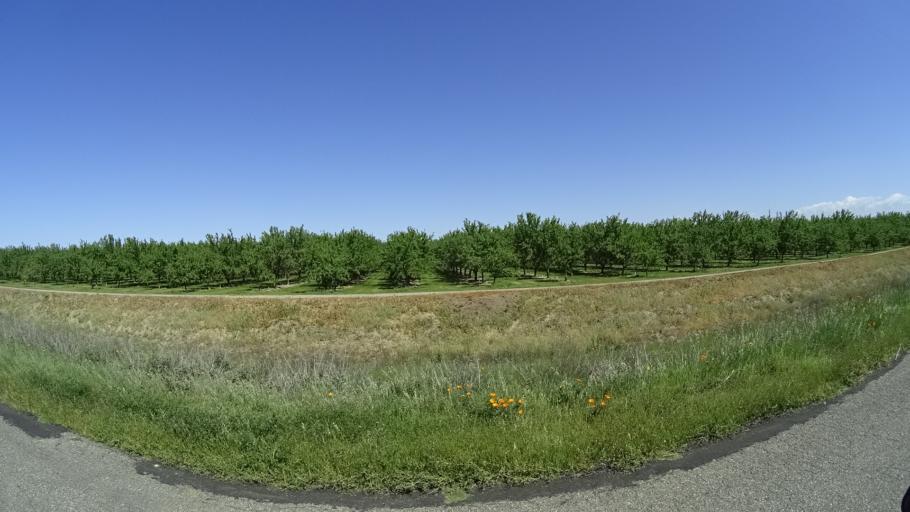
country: US
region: California
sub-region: Glenn County
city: Orland
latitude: 39.6961
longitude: -122.1307
